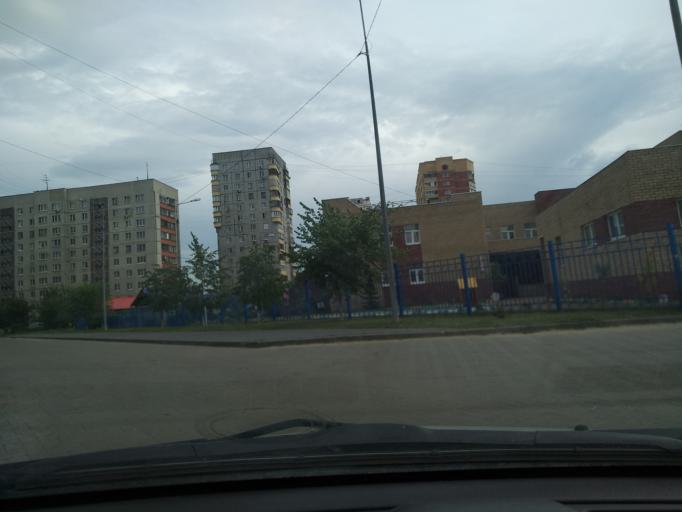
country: RU
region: Moskovskaya
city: Bykovo
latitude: 55.5954
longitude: 38.0905
